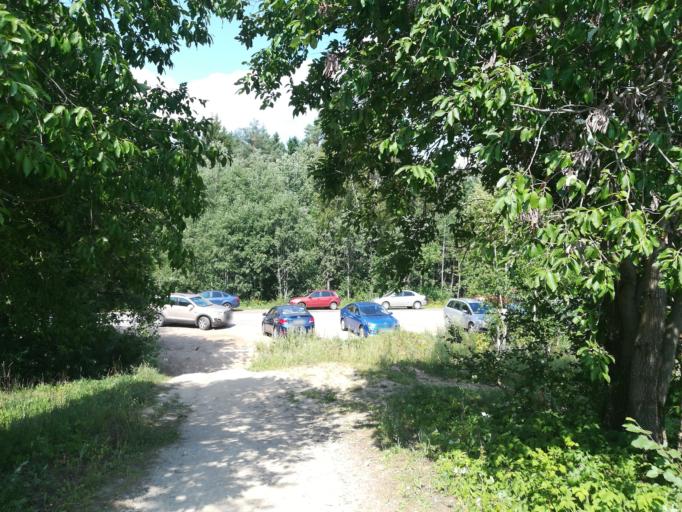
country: RU
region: Leningrad
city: Sista-Palkino
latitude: 59.5925
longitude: 28.8287
